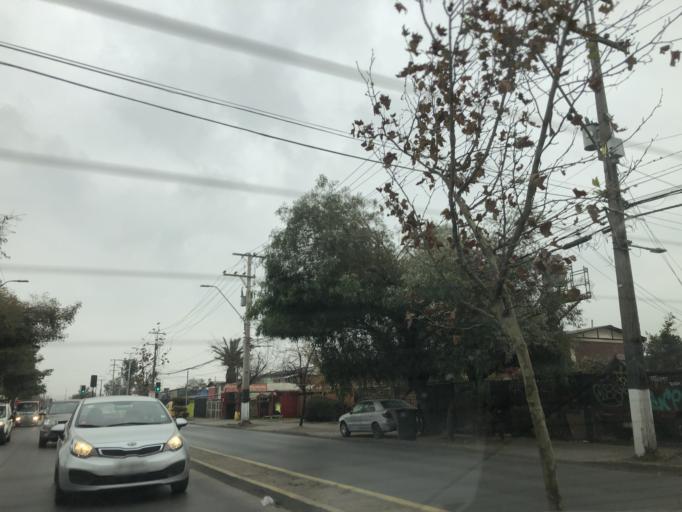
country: CL
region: Santiago Metropolitan
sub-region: Provincia de Santiago
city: La Pintana
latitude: -33.5817
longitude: -70.5996
